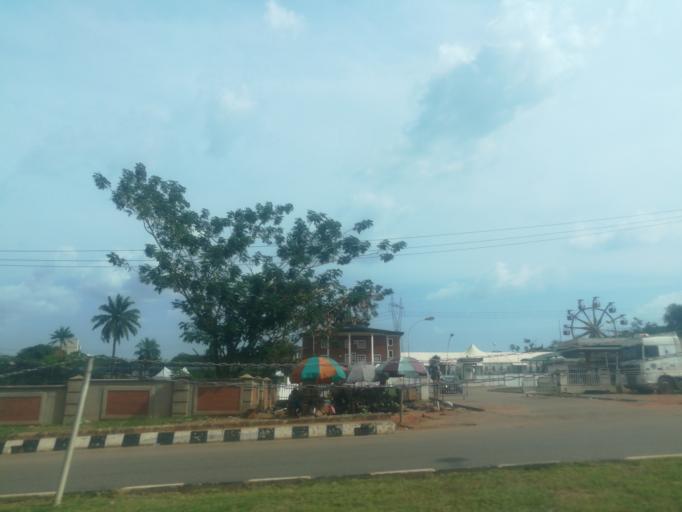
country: NG
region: Ogun
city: Abeokuta
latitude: 7.1272
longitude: 3.3580
